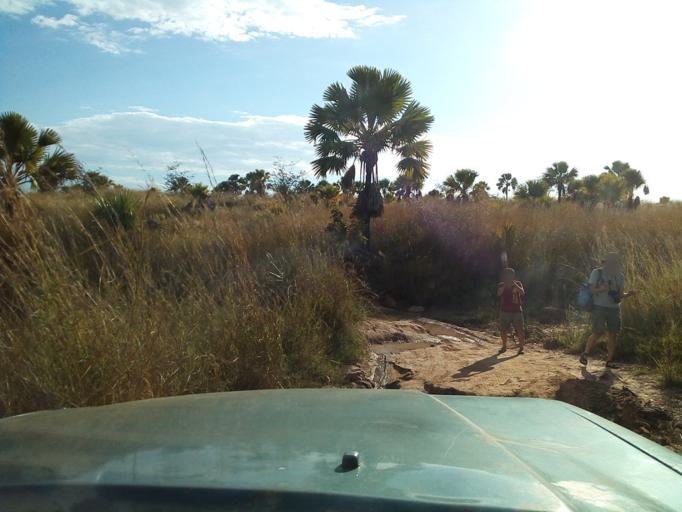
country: MG
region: Boeny
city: Sitampiky
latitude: -16.1479
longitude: 45.5879
